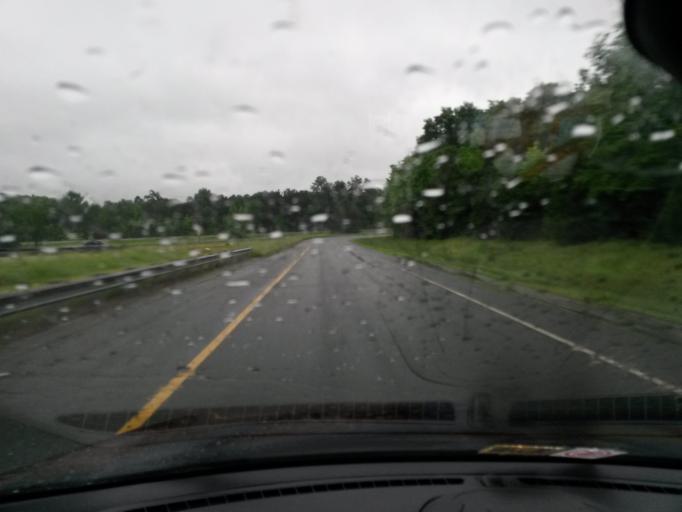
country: US
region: Virginia
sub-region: Henrico County
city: Glen Allen
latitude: 37.6608
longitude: -77.4616
